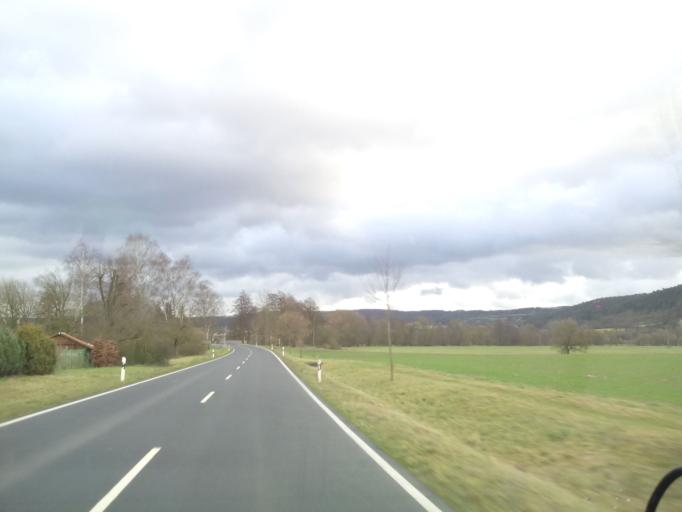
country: DE
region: Bavaria
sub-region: Regierungsbezirk Unterfranken
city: Hammelburg
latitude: 50.1221
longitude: 9.8703
